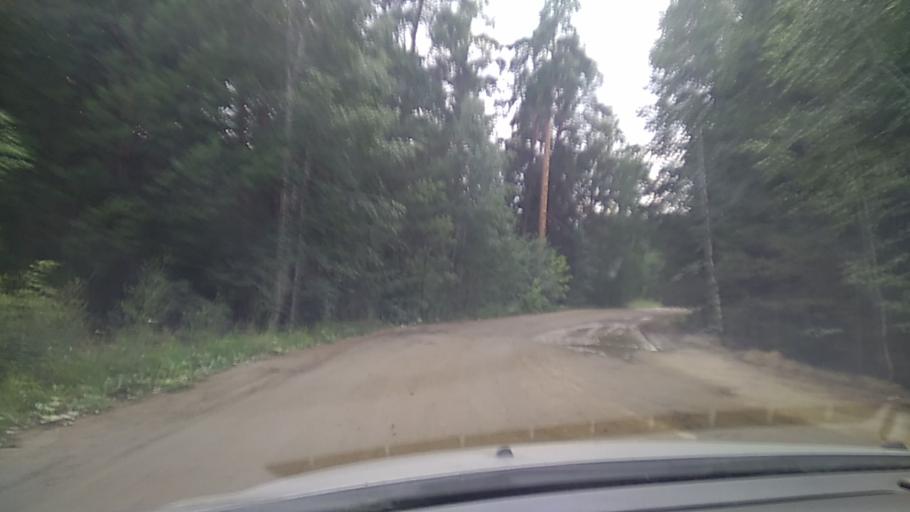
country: RU
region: Chelyabinsk
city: Kyshtym
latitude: 55.6801
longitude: 60.5747
